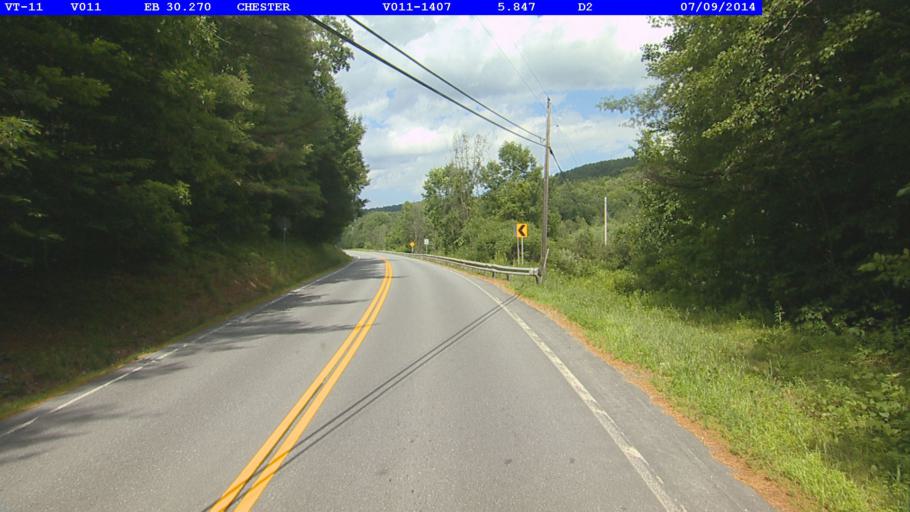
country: US
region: Vermont
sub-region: Windsor County
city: Chester
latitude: 43.2638
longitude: -72.5782
